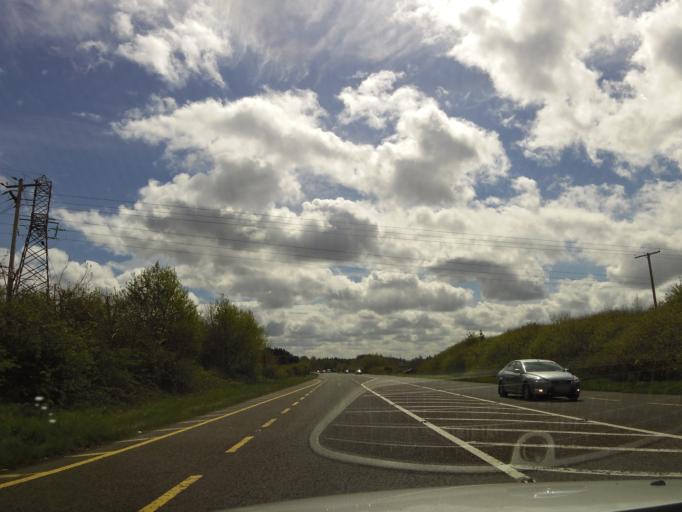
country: IE
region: Connaught
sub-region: Maigh Eo
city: Claremorris
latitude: 53.7098
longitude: -8.9848
